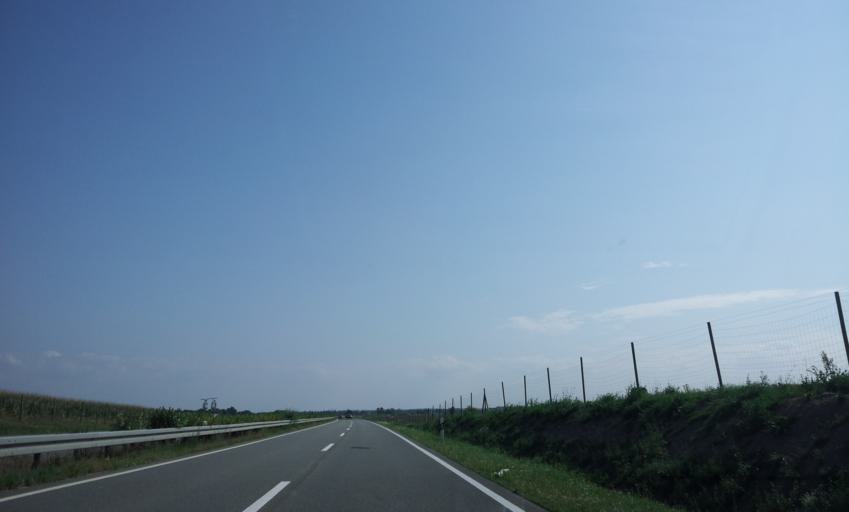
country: DE
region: Mecklenburg-Vorpommern
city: Wittenhagen
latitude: 54.1348
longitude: 13.1595
